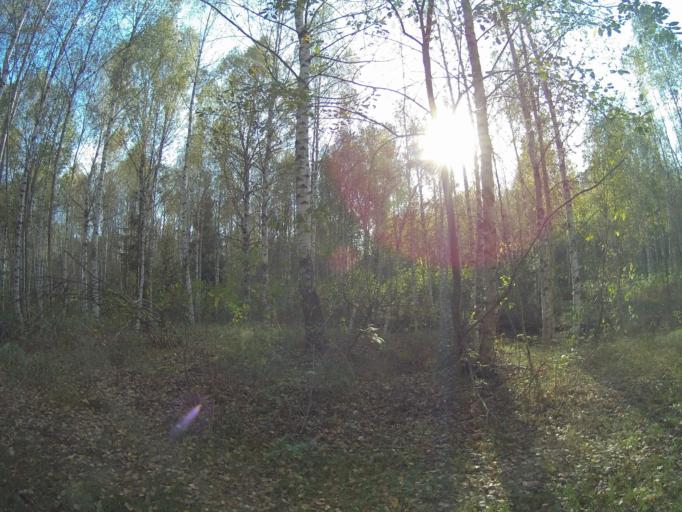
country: RU
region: Vladimir
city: Urshel'skiy
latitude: 55.8325
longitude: 40.1862
